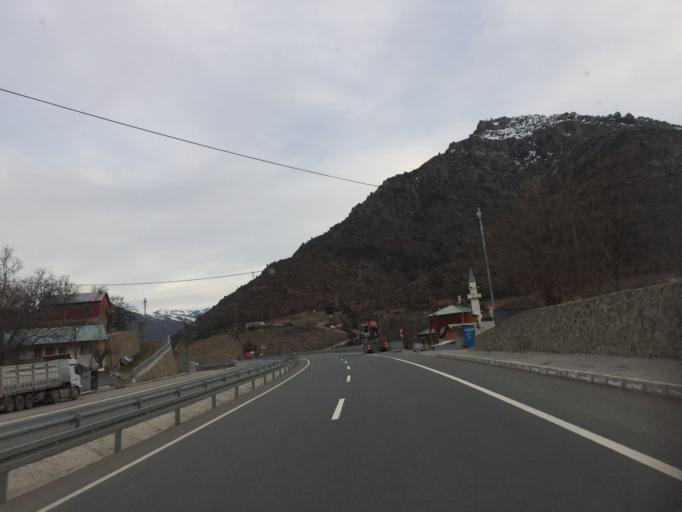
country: TR
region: Gumushane
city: Torul
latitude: 40.5380
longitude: 39.3266
